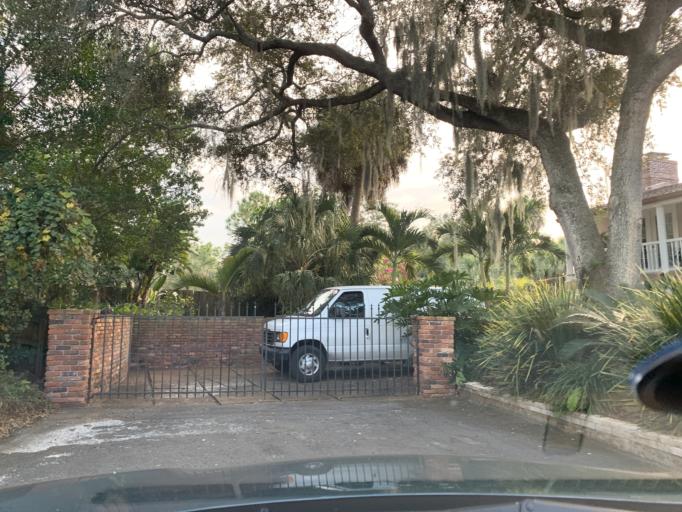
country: US
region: Florida
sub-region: Pinellas County
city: Bay Pines
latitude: 27.8072
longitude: -82.7560
